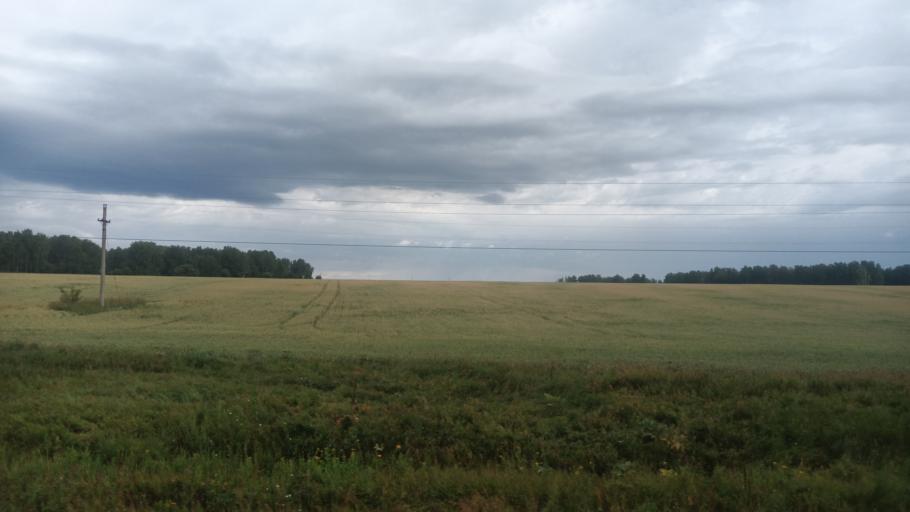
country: RU
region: Altai Krai
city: Nalobikha
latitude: 53.2326
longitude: 84.5087
